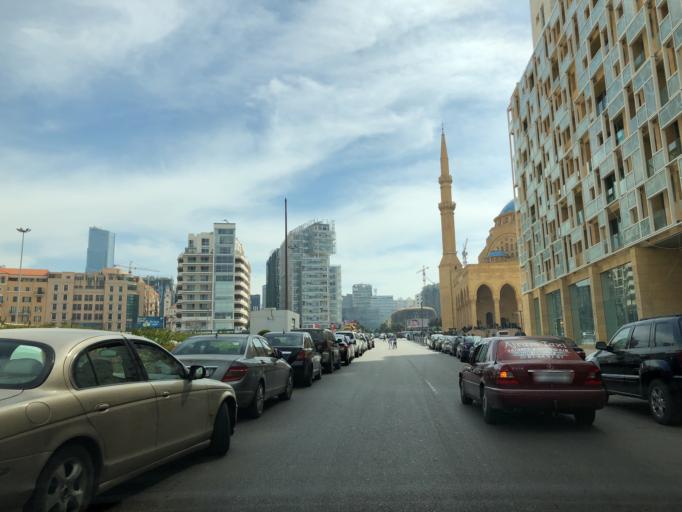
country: LB
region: Beyrouth
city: Beirut
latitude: 33.8967
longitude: 35.5069
